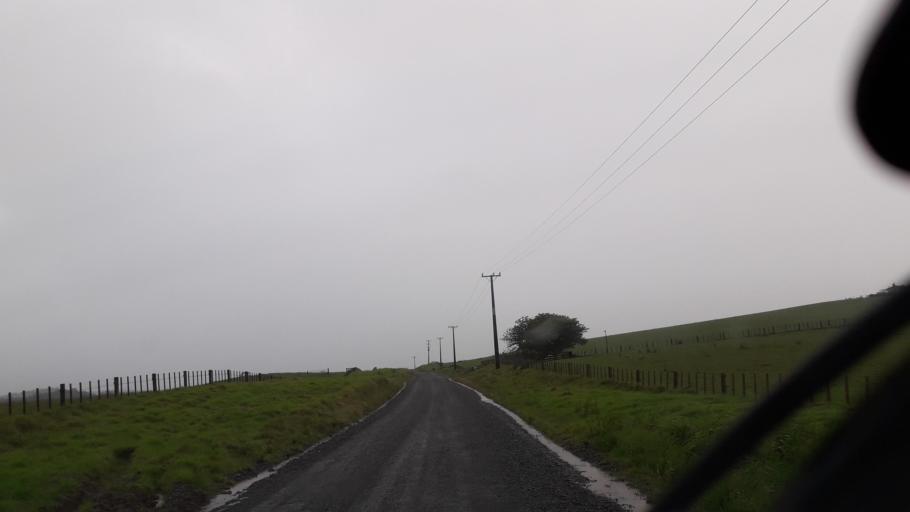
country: NZ
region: Northland
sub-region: Far North District
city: Kerikeri
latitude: -35.1434
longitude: 174.0372
